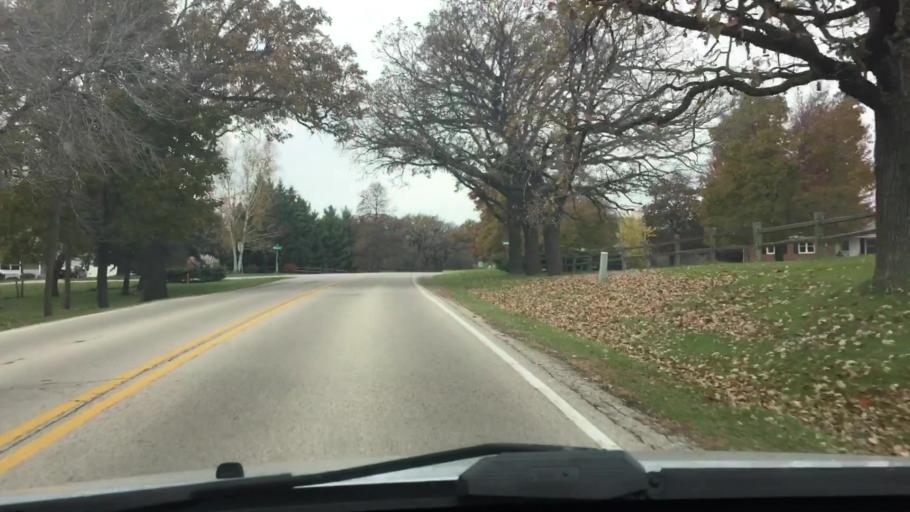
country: US
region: Wisconsin
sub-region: Waukesha County
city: North Prairie
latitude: 42.8983
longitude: -88.3992
